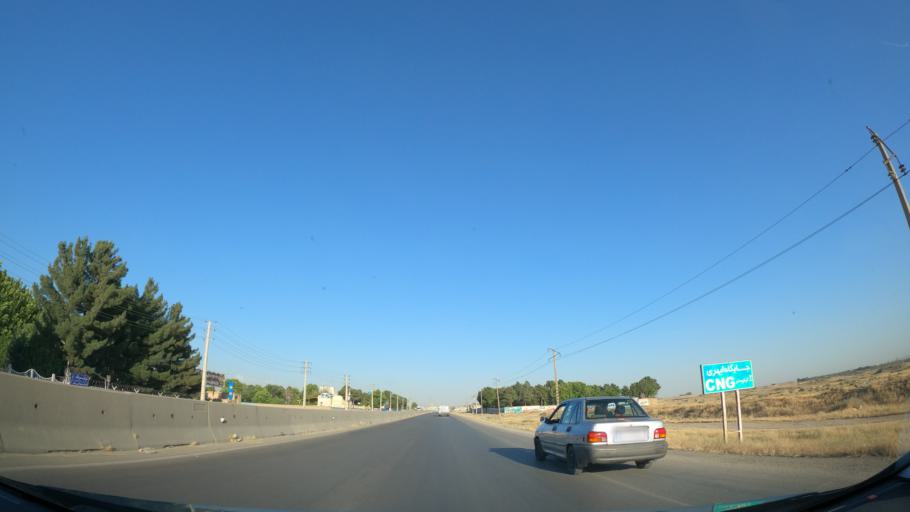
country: IR
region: Alborz
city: Hashtgerd
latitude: 35.9224
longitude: 50.7440
